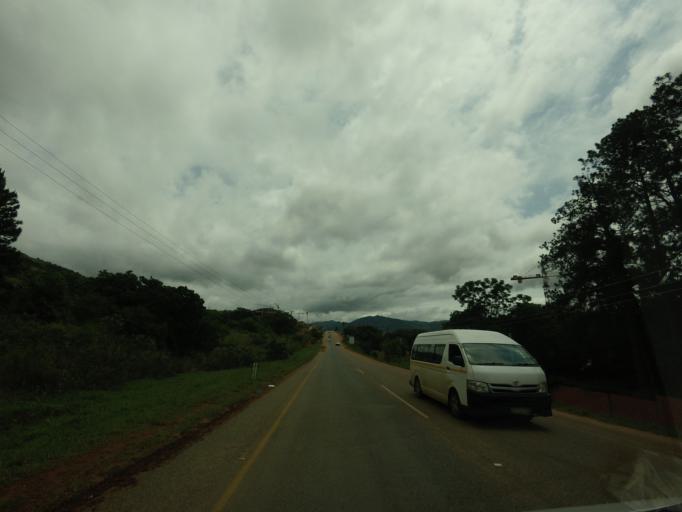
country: SZ
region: Hhohho
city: Lobamba
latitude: -26.4204
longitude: 31.1774
